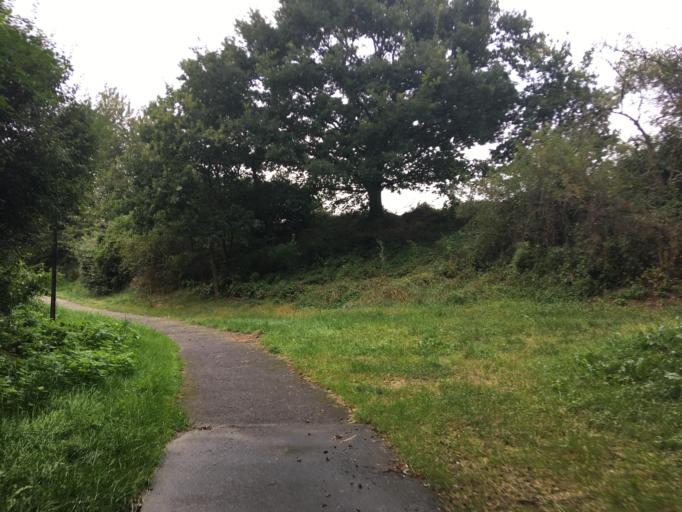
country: DE
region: Saxony
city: Dohna
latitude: 50.9439
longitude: 13.8929
